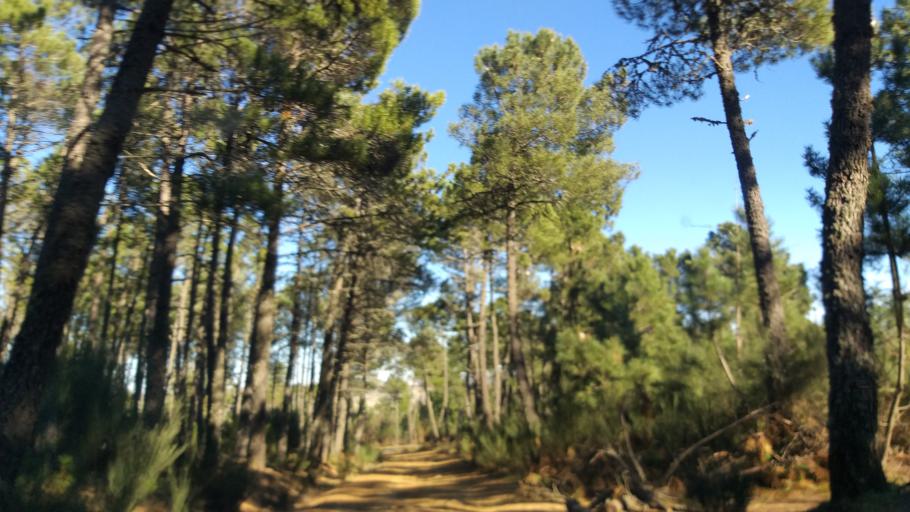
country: PT
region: Guarda
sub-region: Celorico da Beira
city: Celorico da Beira
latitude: 40.5146
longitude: -7.4056
